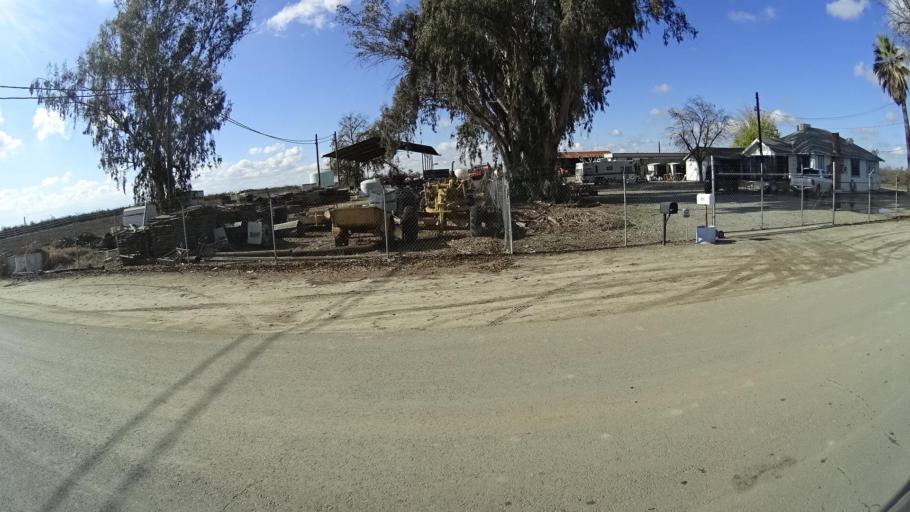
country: US
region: California
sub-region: Kern County
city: Delano
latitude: 35.7444
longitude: -119.3657
